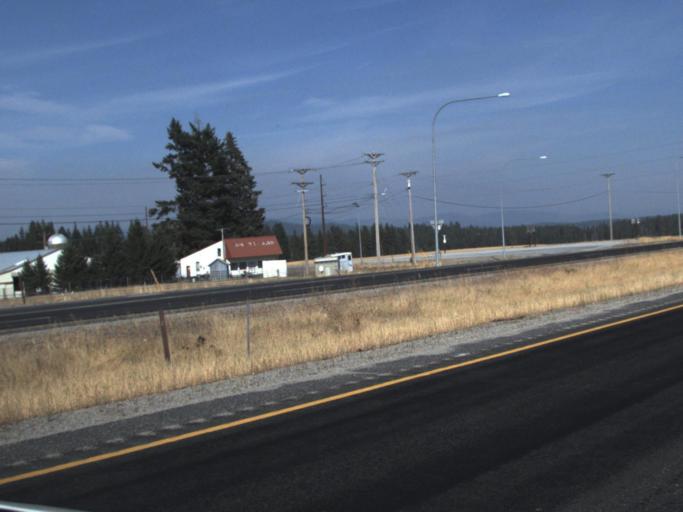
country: US
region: Washington
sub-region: Spokane County
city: Deer Park
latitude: 48.0969
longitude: -117.2807
